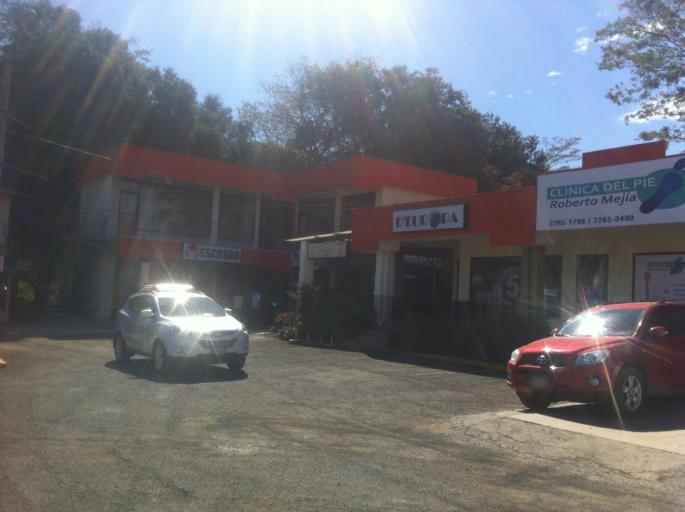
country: NI
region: Managua
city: Ciudad Sandino
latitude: 12.1087
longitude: -86.3159
